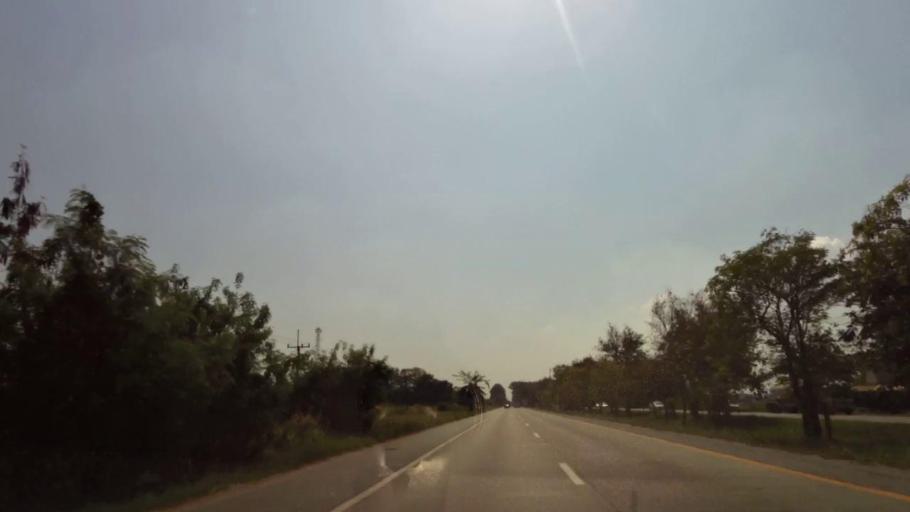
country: TH
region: Phichit
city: Wachira Barami
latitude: 16.5840
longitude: 100.1474
